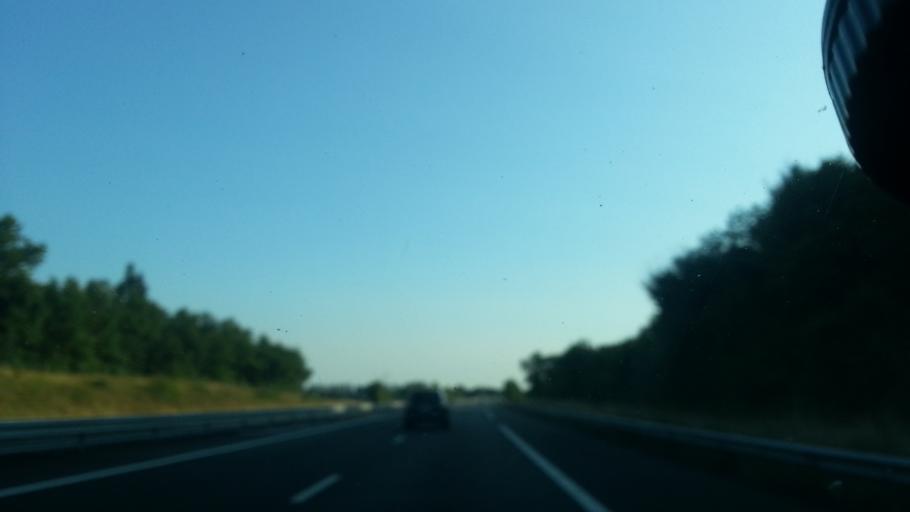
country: FR
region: Poitou-Charentes
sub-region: Departement des Deux-Sevres
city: Beauvoir-sur-Niort
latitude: 46.1398
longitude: -0.5269
